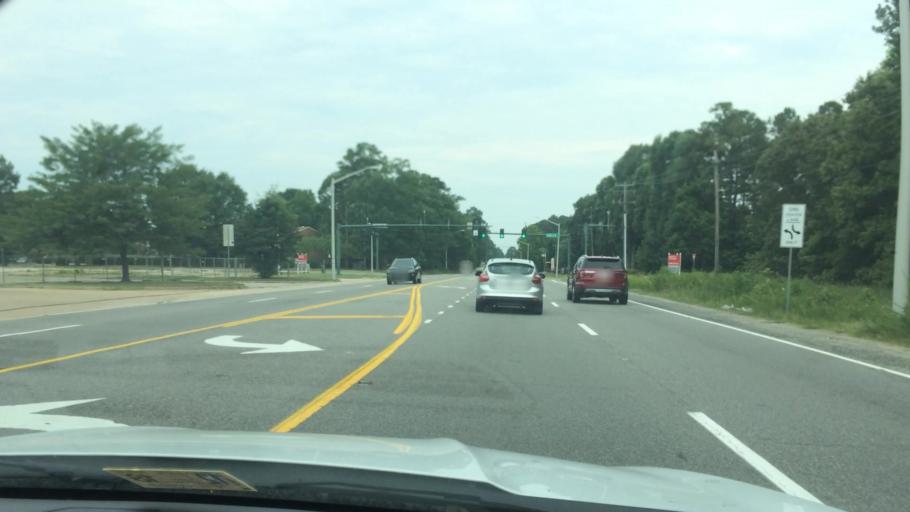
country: US
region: Virginia
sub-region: York County
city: Yorktown
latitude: 37.1664
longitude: -76.5418
